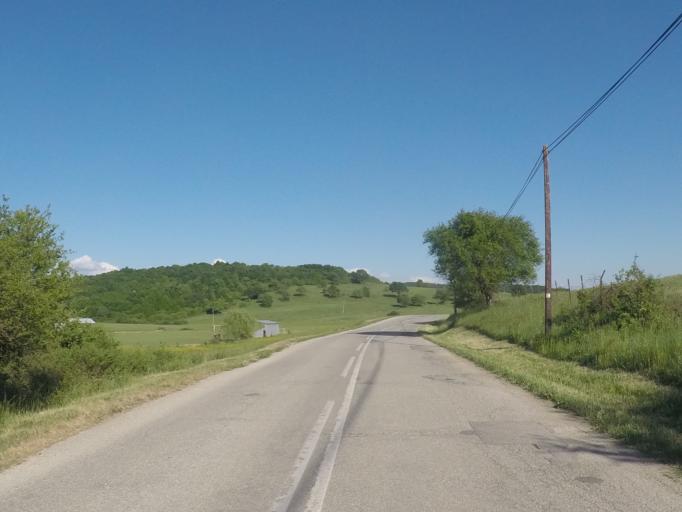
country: HU
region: Borsod-Abauj-Zemplen
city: Putnok
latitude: 48.4894
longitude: 20.4459
